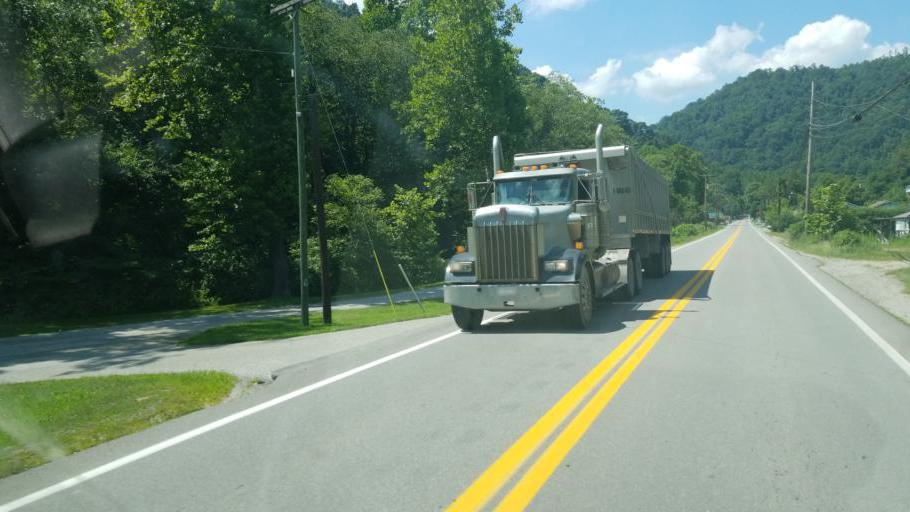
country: US
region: West Virginia
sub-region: Kanawha County
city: Chesapeake
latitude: 38.1780
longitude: -81.4650
